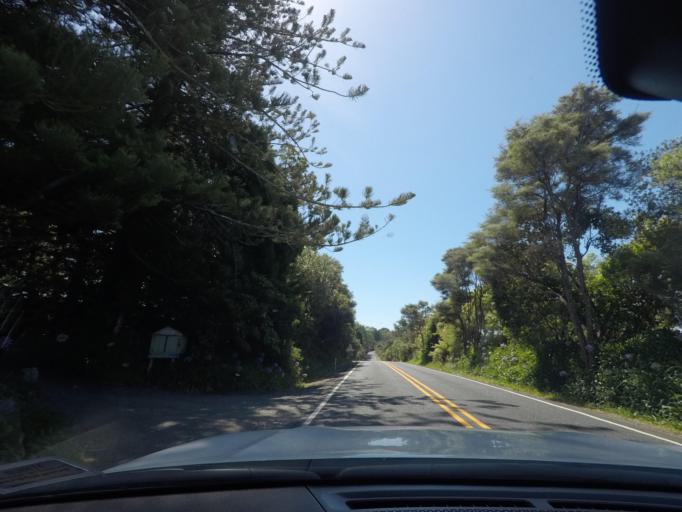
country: NZ
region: Auckland
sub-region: Auckland
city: Parakai
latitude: -36.6197
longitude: 174.3465
